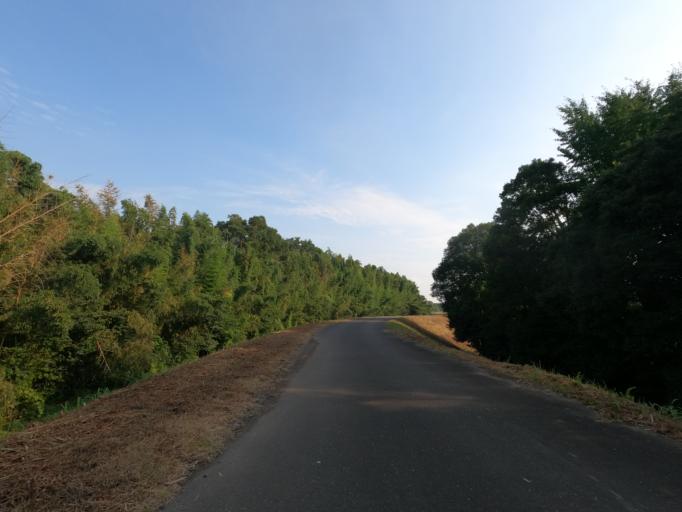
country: JP
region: Ibaraki
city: Mitsukaido
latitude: 36.0050
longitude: 139.9739
